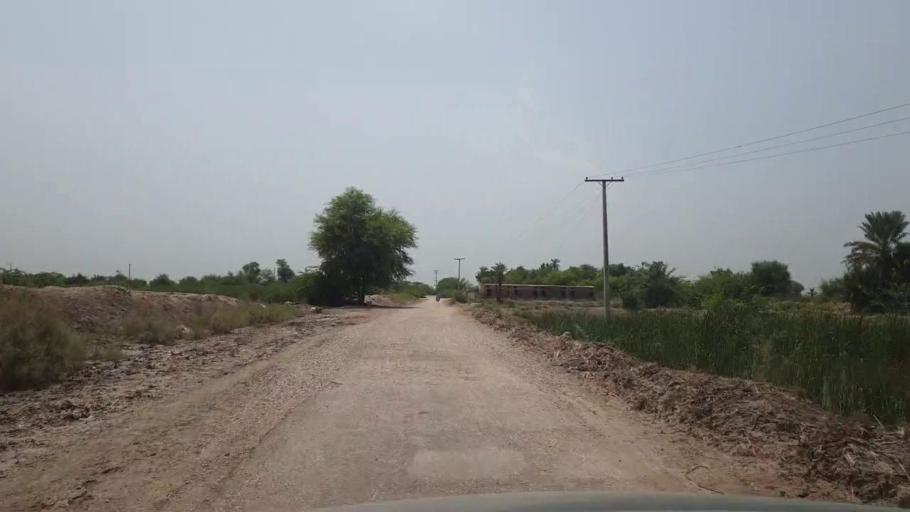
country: PK
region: Sindh
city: Garhi Yasin
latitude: 27.8792
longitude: 68.4953
